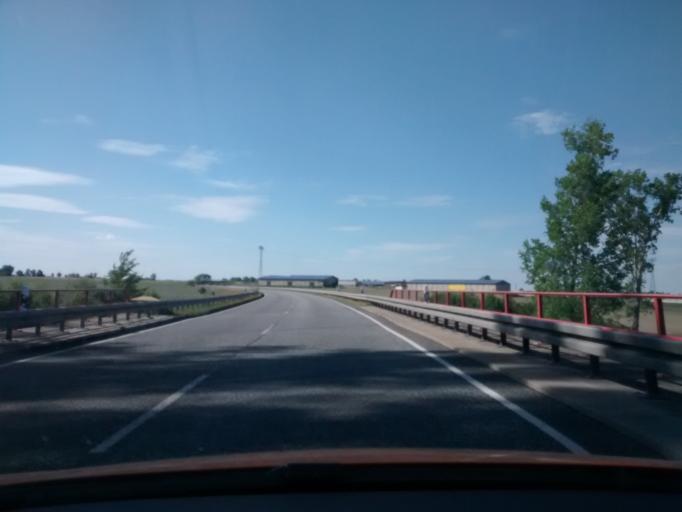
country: DE
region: Brandenburg
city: Juterbog
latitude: 52.0010
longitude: 13.1040
